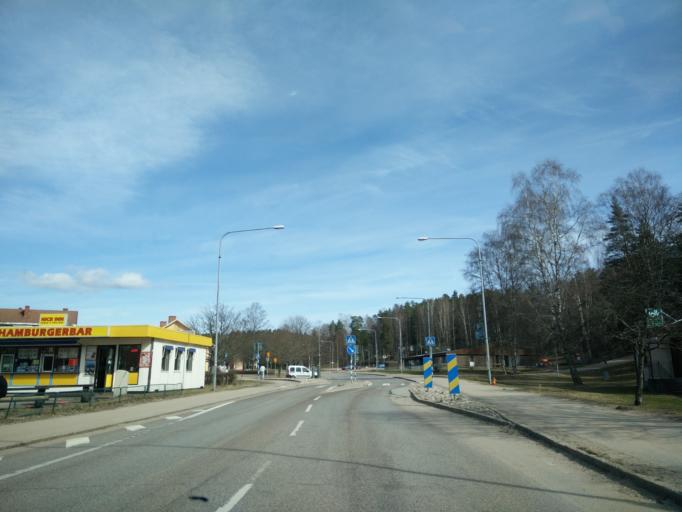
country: SE
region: Vaermland
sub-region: Hagfors Kommun
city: Hagfors
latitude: 60.0322
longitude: 13.7030
